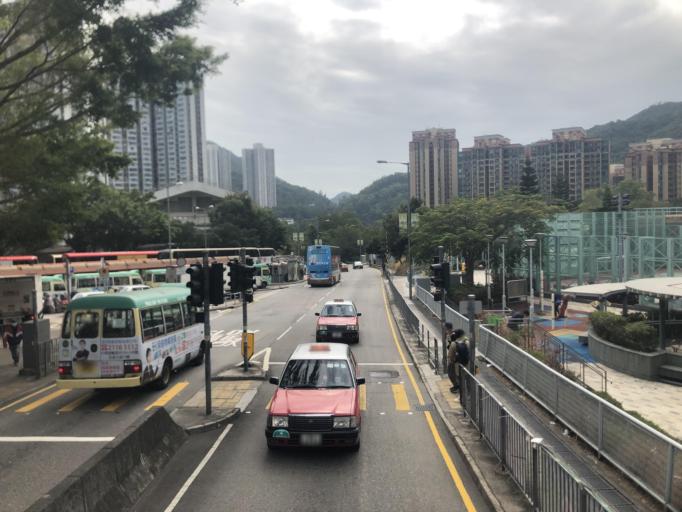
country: HK
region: Tsuen Wan
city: Tsuen Wan
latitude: 22.3561
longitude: 114.0974
